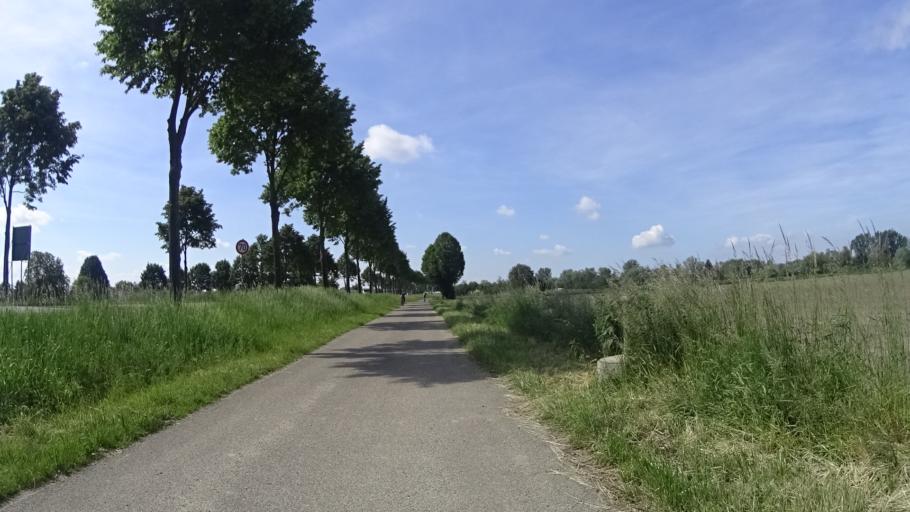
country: DE
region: Baden-Wuerttemberg
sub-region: Freiburg Region
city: Kehl
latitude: 48.5176
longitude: 7.8208
